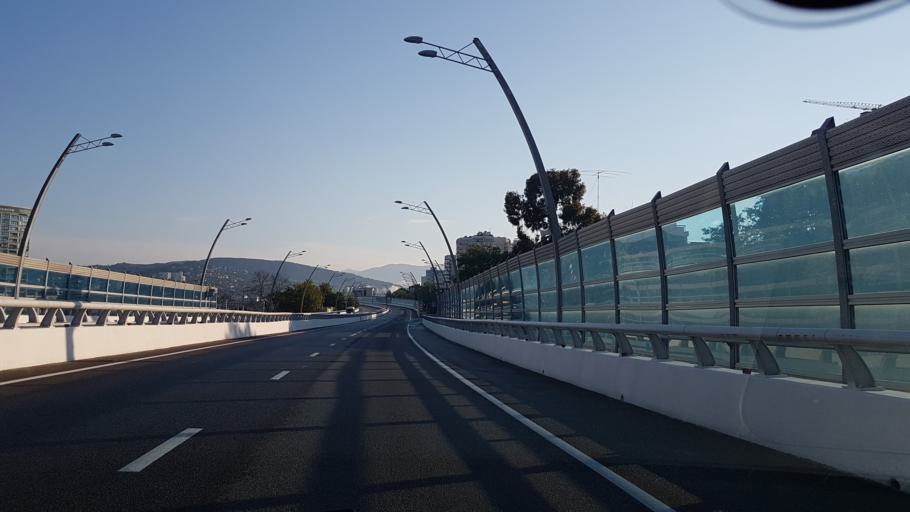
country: RU
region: Krasnodarskiy
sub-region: Sochi City
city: Sochi
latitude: 43.5918
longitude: 39.7306
